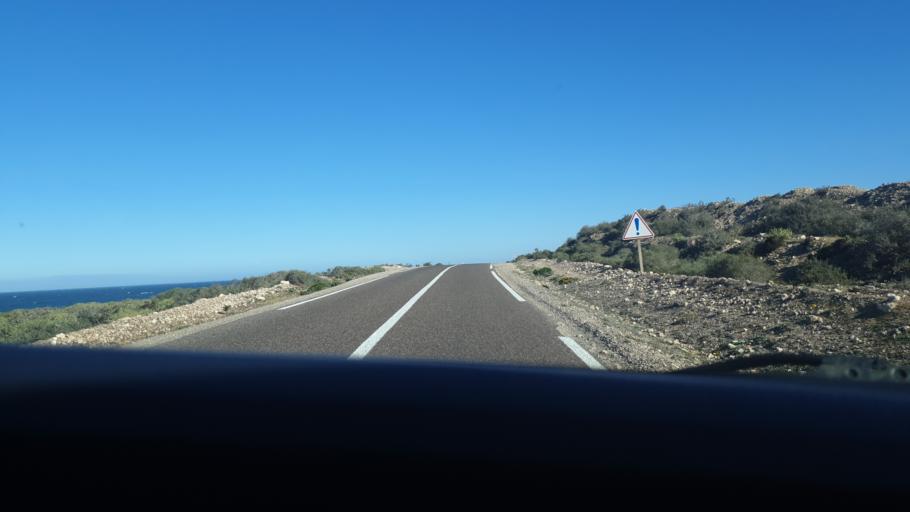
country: MA
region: Souss-Massa-Draa
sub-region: Agadir-Ida-ou-Tnan
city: Tamri
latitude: 30.6601
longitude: -9.8850
